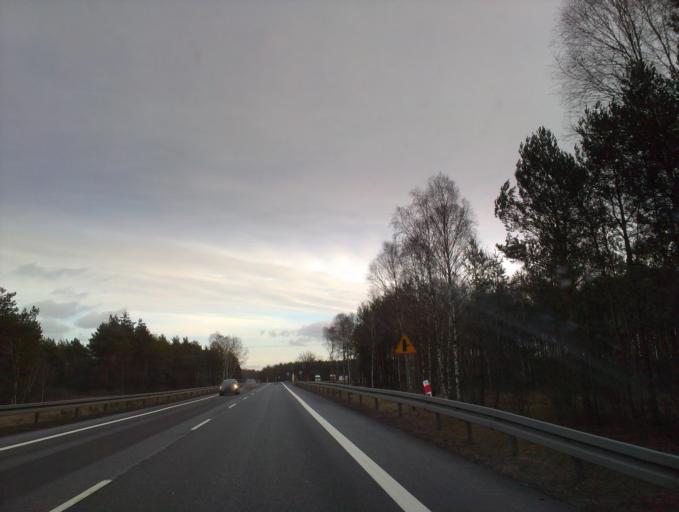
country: PL
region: Masovian Voivodeship
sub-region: Powiat sierpecki
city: Szczutowo
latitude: 52.8934
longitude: 19.5559
